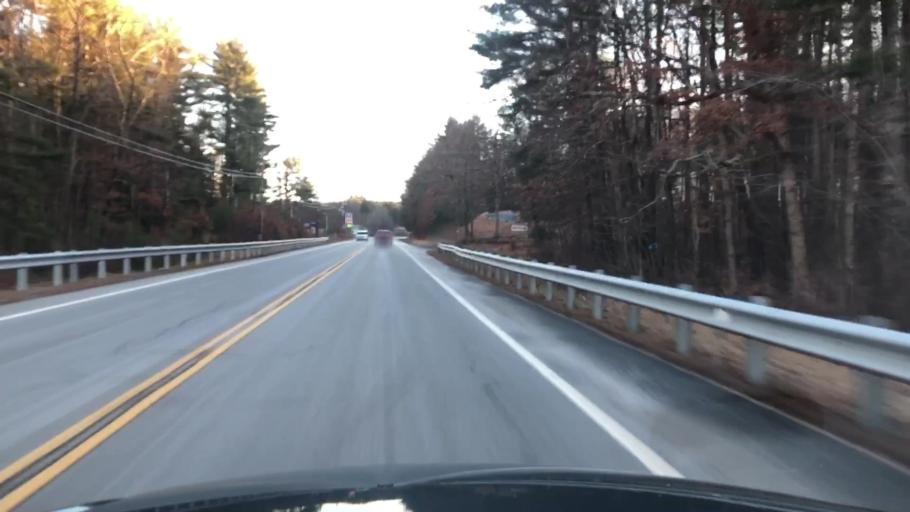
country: US
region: New Hampshire
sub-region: Hillsborough County
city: Brookline
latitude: 42.7258
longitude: -71.6631
